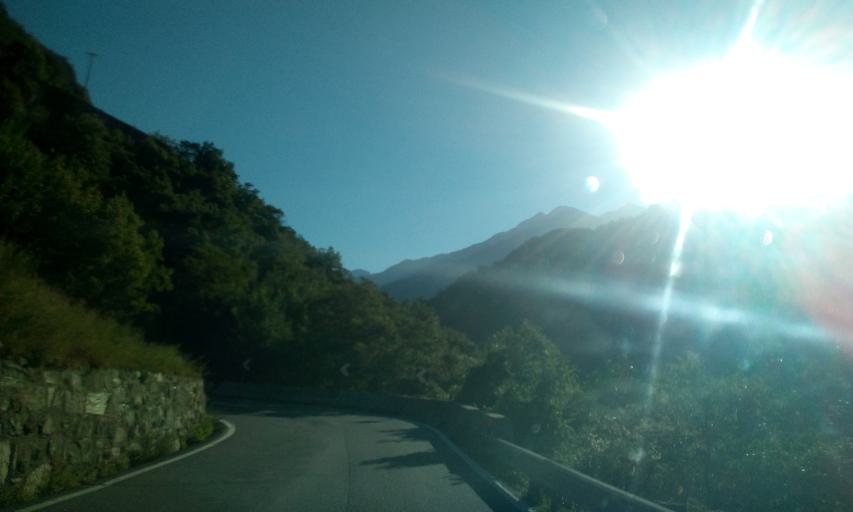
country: IT
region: Aosta Valley
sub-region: Valle d'Aosta
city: Verres
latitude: 45.6744
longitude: 7.6969
